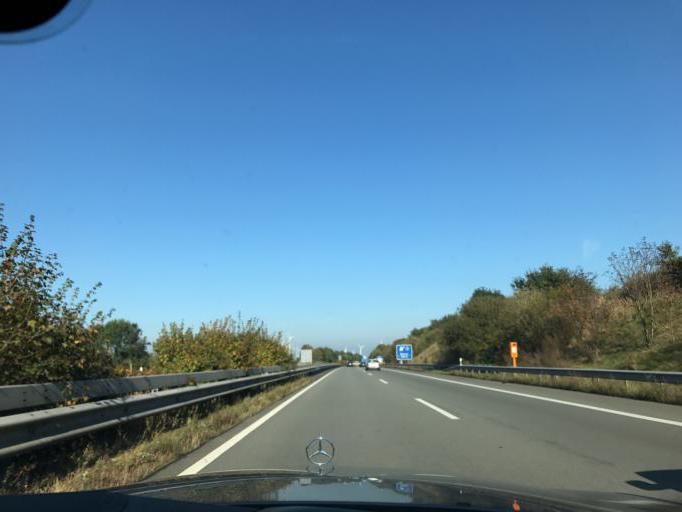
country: DE
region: Lower Saxony
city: Bunde
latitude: 53.1702
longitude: 7.2871
